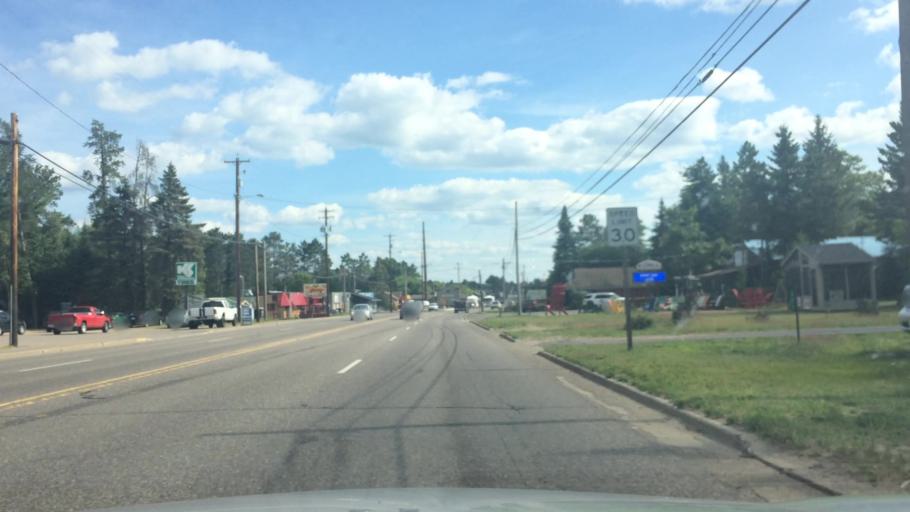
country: US
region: Wisconsin
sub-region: Vilas County
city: Lac du Flambeau
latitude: 45.9012
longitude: -89.6976
